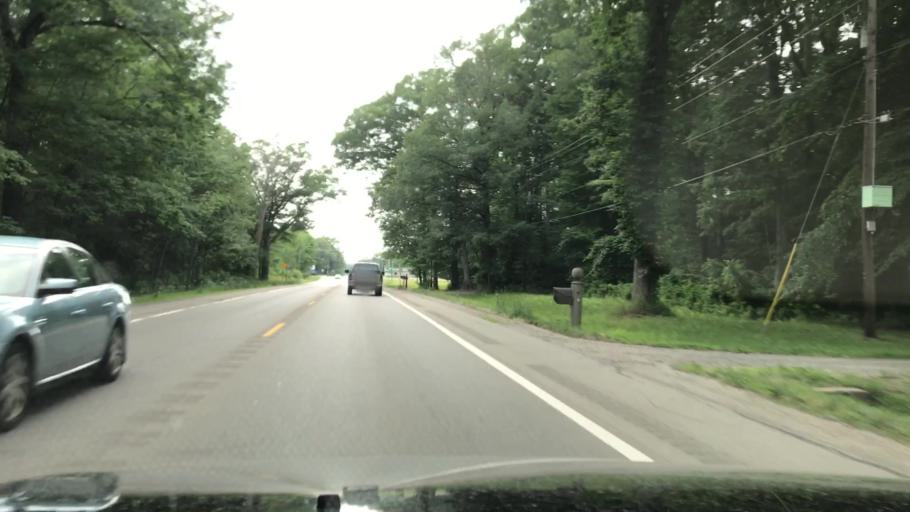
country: US
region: Michigan
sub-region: Ottawa County
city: Spring Lake
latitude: 43.0739
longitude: -86.1419
